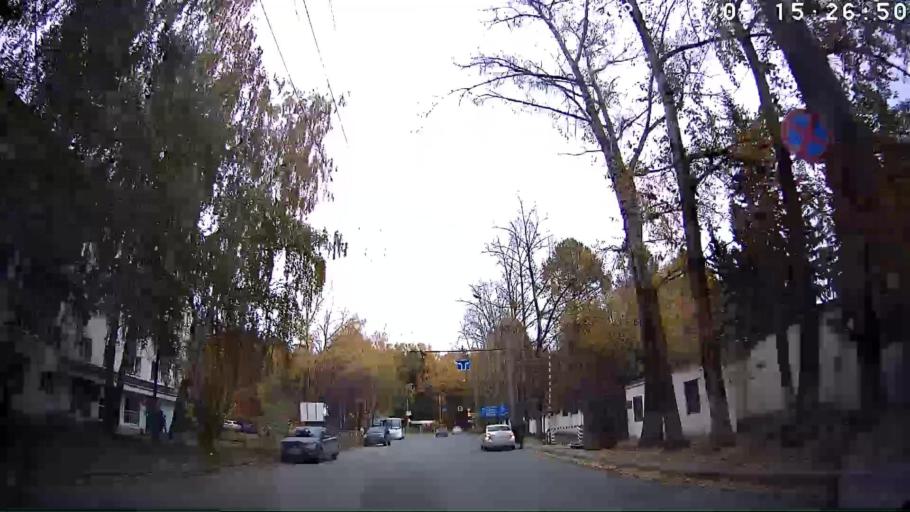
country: RU
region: Mariy-El
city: Yoshkar-Ola
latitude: 56.6221
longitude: 47.9512
